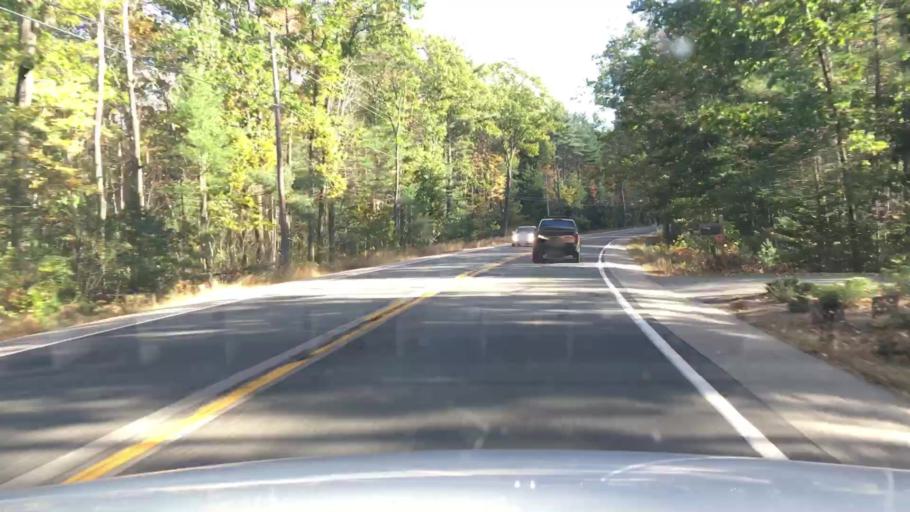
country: US
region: Maine
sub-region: York County
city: South Sanford
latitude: 43.3739
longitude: -70.6759
